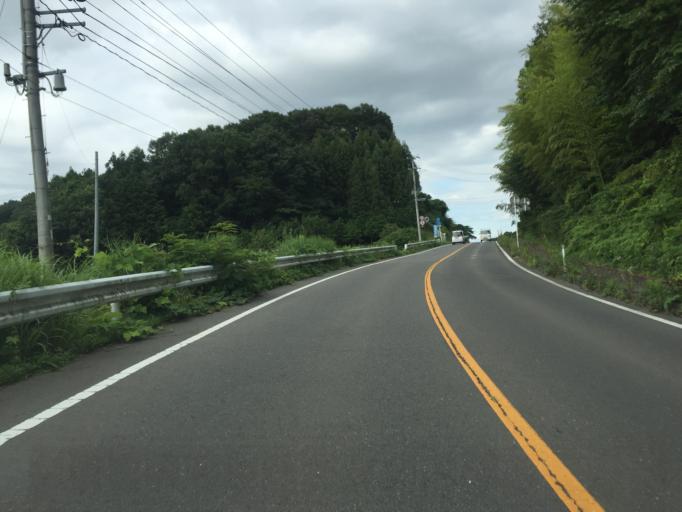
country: JP
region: Fukushima
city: Motomiya
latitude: 37.5518
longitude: 140.4076
